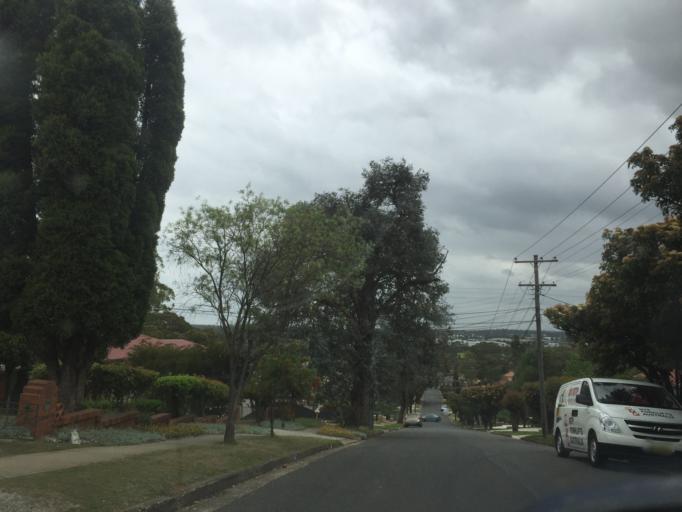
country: AU
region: New South Wales
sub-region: Blacktown
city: Doonside
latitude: -33.7792
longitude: 150.8904
